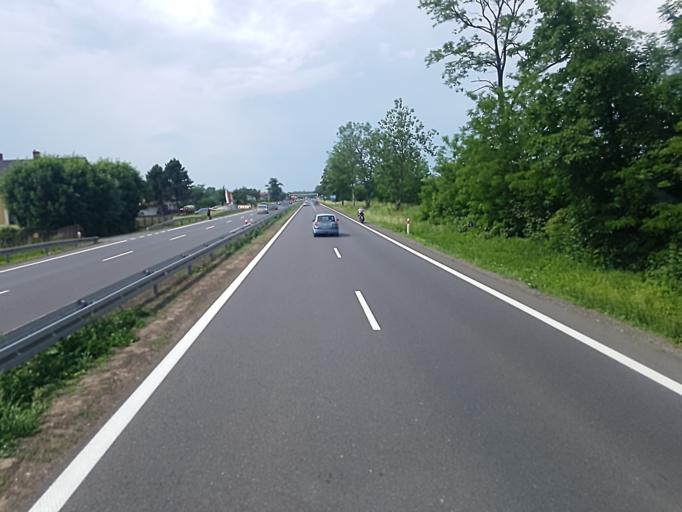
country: PL
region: Silesian Voivodeship
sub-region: Powiat cieszynski
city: Ochaby
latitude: 49.8371
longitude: 18.7737
